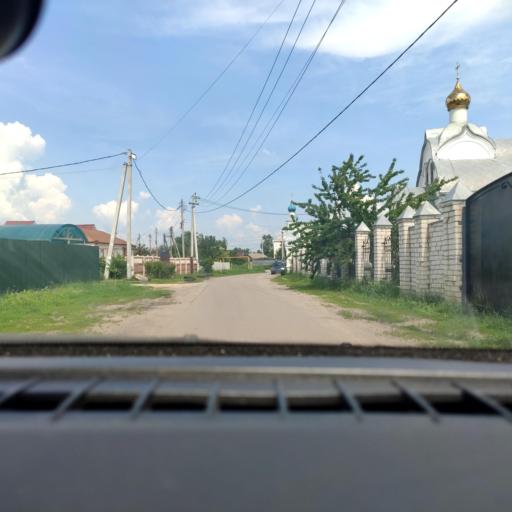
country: RU
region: Voronezj
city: Novaya Usman'
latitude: 51.6805
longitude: 39.3687
